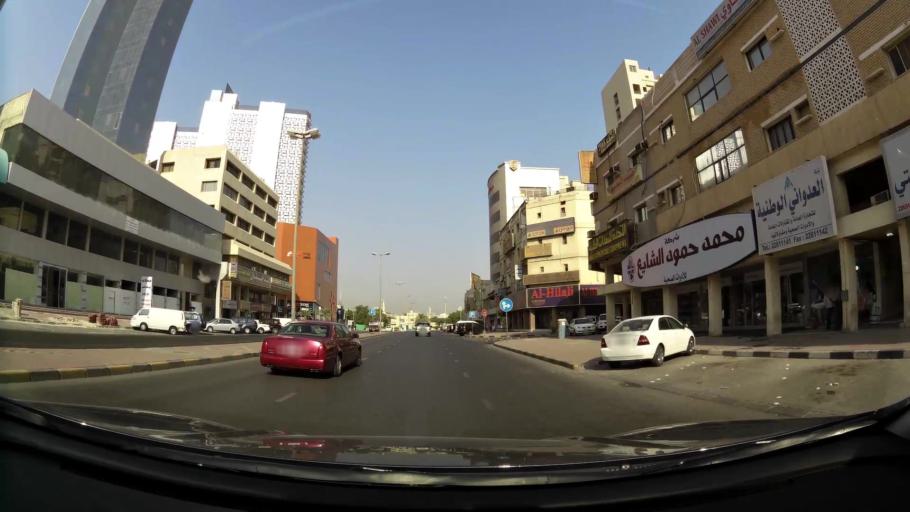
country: KW
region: Muhafazat Hawalli
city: Hawalli
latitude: 29.3464
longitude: 48.0138
